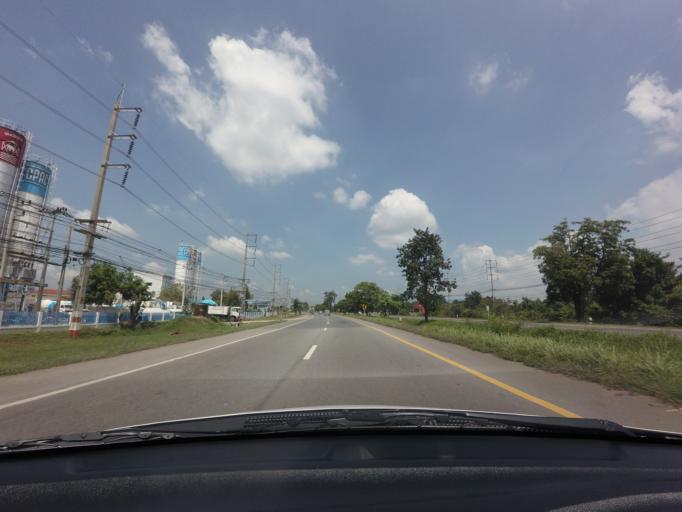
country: TH
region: Prachin Buri
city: Si Maha Phot
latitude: 13.8694
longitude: 101.5596
